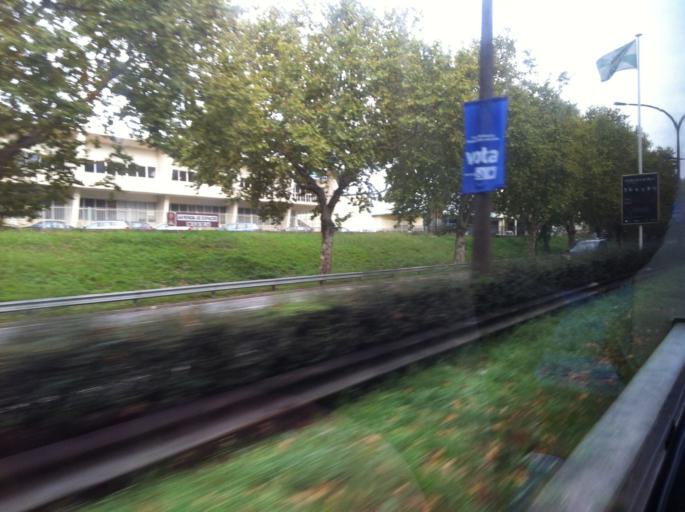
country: PT
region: Porto
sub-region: Matosinhos
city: Senhora da Hora
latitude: 41.1750
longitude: -8.6518
